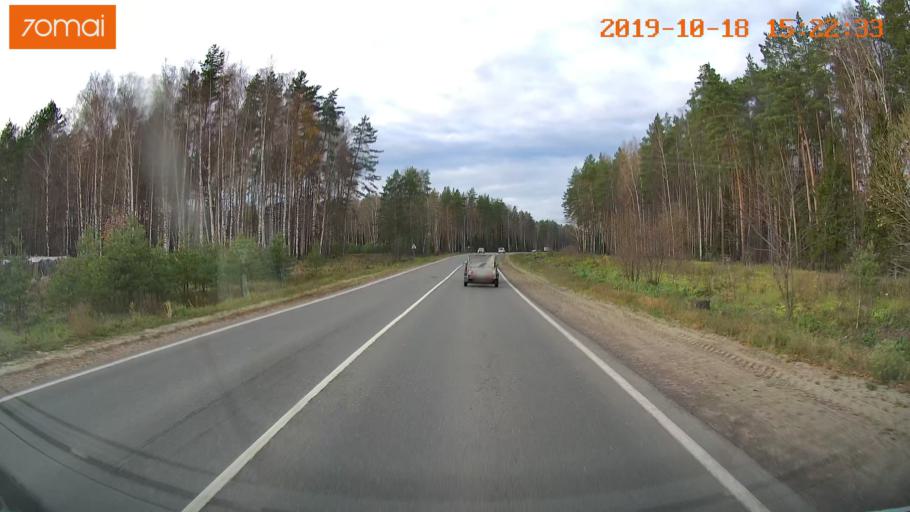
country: RU
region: Vladimir
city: Anopino
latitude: 55.7088
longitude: 40.7303
